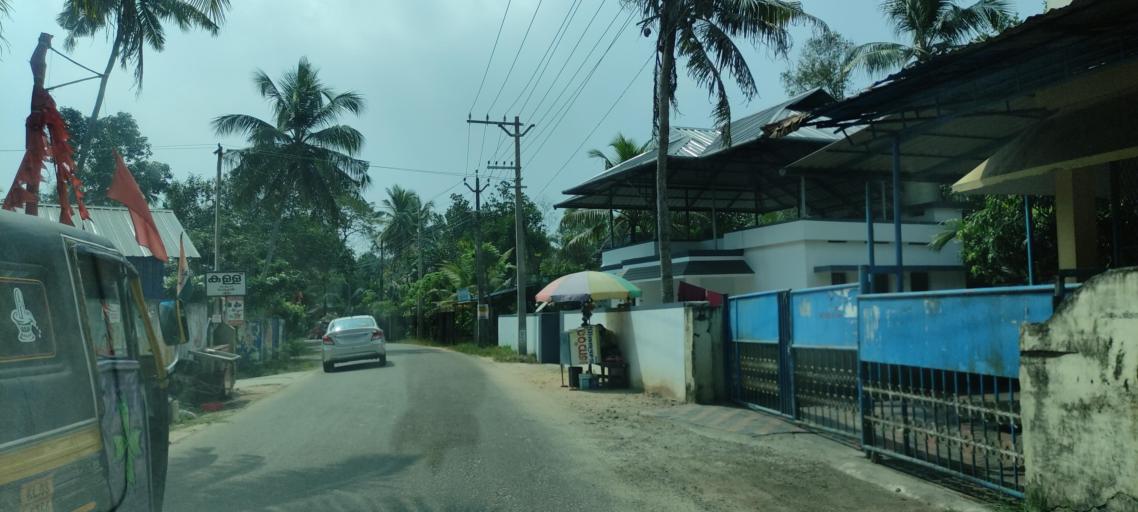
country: IN
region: Kerala
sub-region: Alappuzha
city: Shertallai
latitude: 9.6227
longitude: 76.3495
